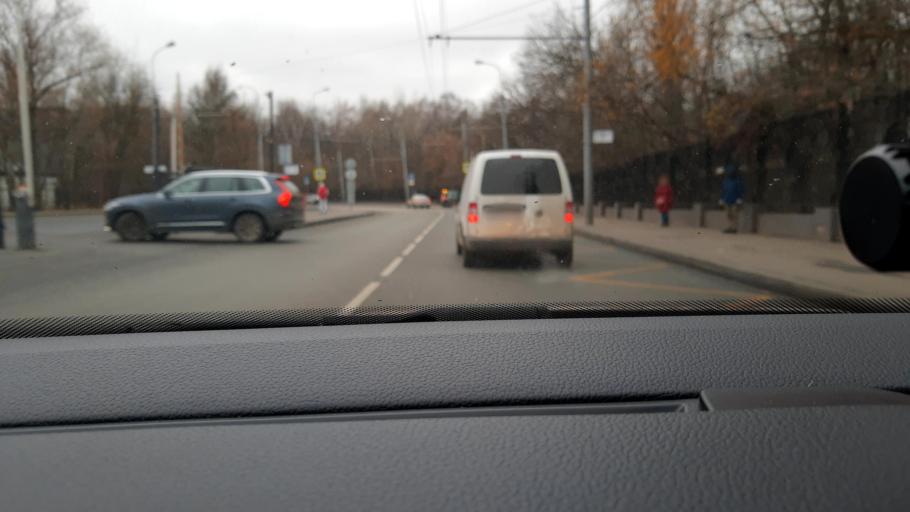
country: RU
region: Moskovskaya
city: Fili
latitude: 55.7514
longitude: 37.4928
